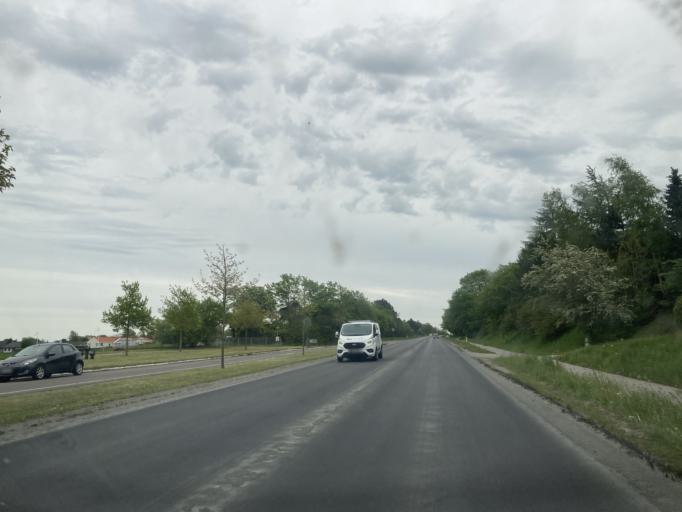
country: DK
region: Zealand
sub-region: Roskilde Kommune
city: Svogerslev
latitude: 55.6332
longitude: 11.9980
